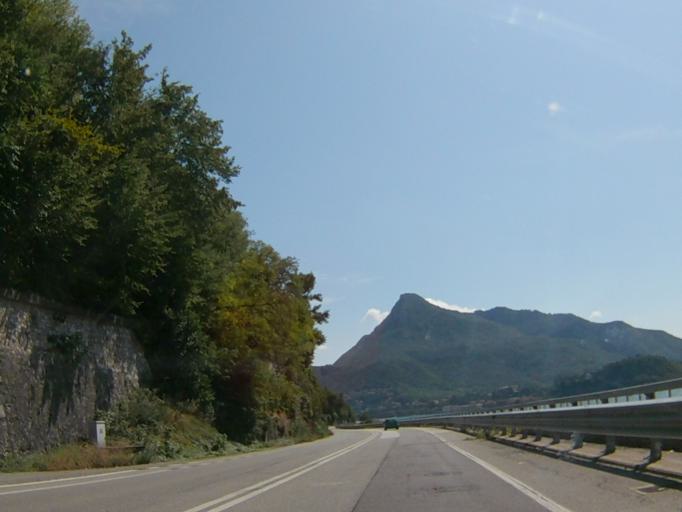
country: IT
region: Lombardy
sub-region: Provincia di Lecco
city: Lecco
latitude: 45.8731
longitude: 9.3776
